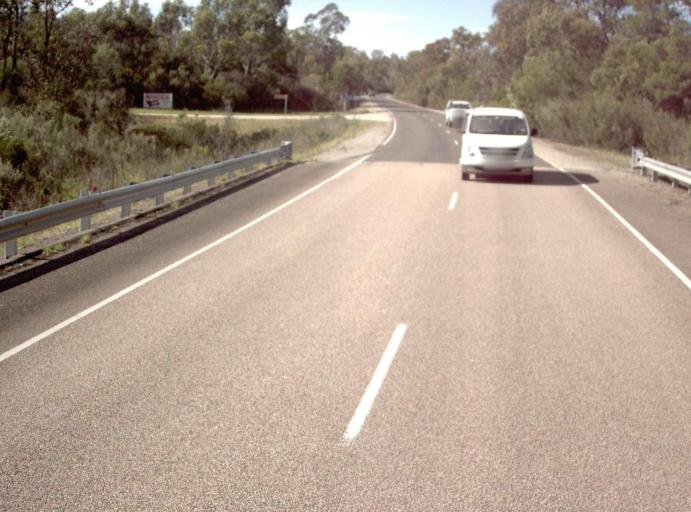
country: AU
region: Victoria
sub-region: East Gippsland
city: Lakes Entrance
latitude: -37.5958
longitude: 148.1206
